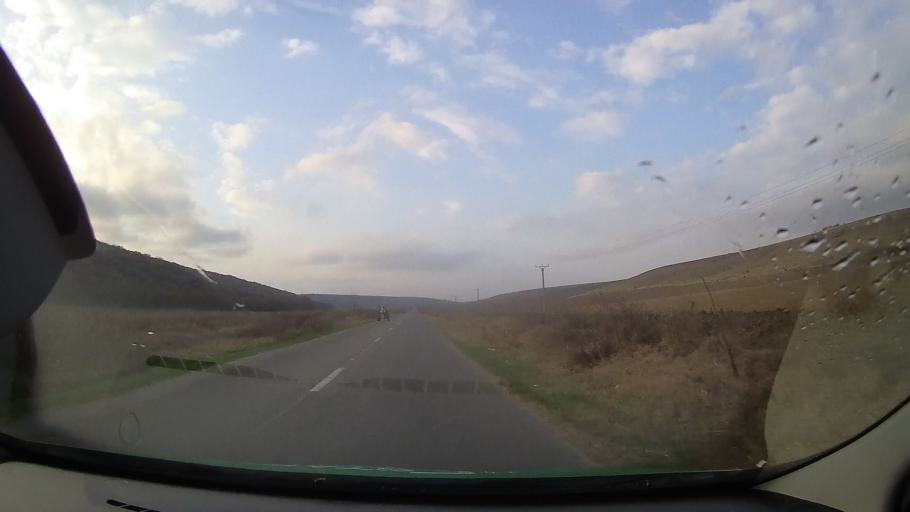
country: RO
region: Constanta
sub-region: Comuna Dobromir
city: Dobromir
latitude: 44.0278
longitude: 27.8636
